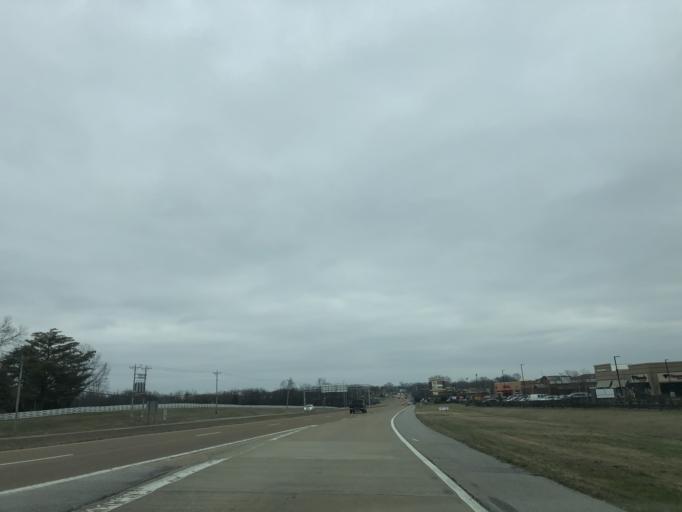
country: US
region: Tennessee
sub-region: Maury County
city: Spring Hill
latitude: 35.7405
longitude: -86.9438
